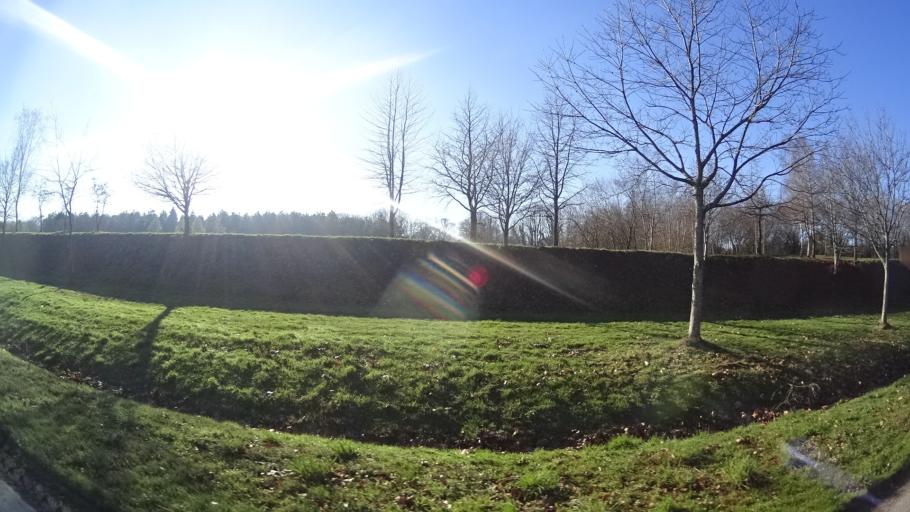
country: FR
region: Brittany
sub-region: Departement du Morbihan
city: Allaire
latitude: 47.6389
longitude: -2.1501
